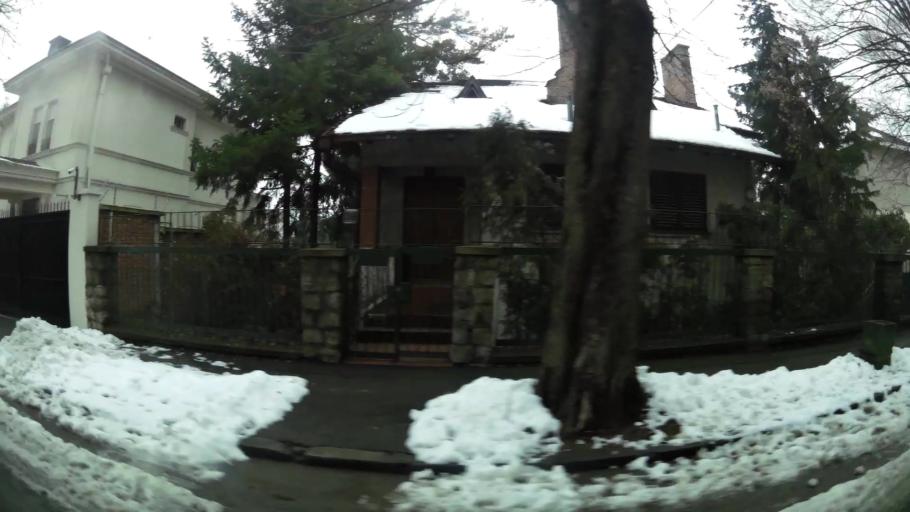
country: RS
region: Central Serbia
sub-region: Belgrade
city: Cukarica
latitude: 44.7922
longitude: 20.4328
